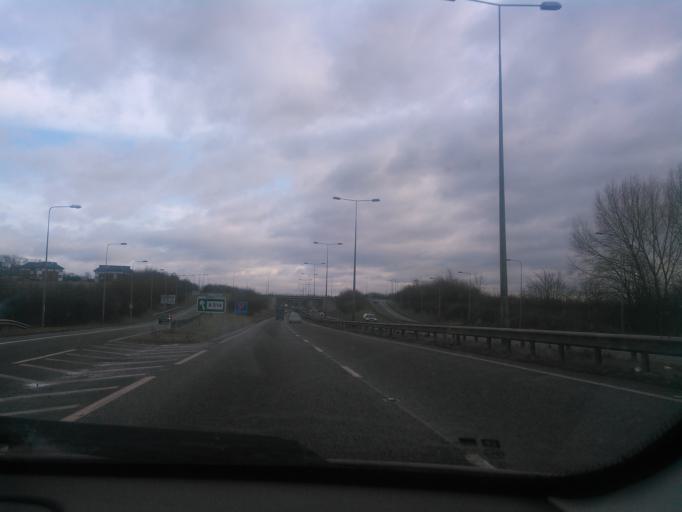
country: GB
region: England
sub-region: Derbyshire
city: Melbourne
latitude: 52.8618
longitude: -1.4459
